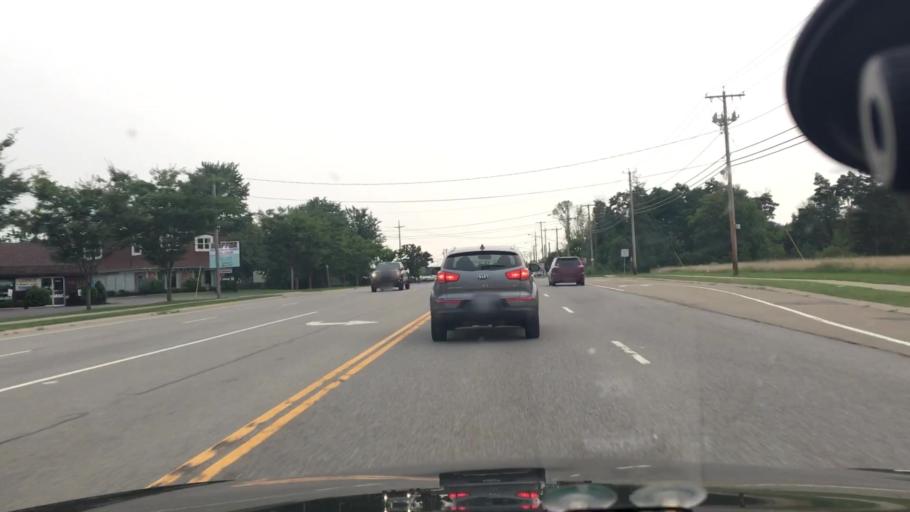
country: US
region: New York
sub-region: Erie County
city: Hamburg
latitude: 42.7528
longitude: -78.8488
